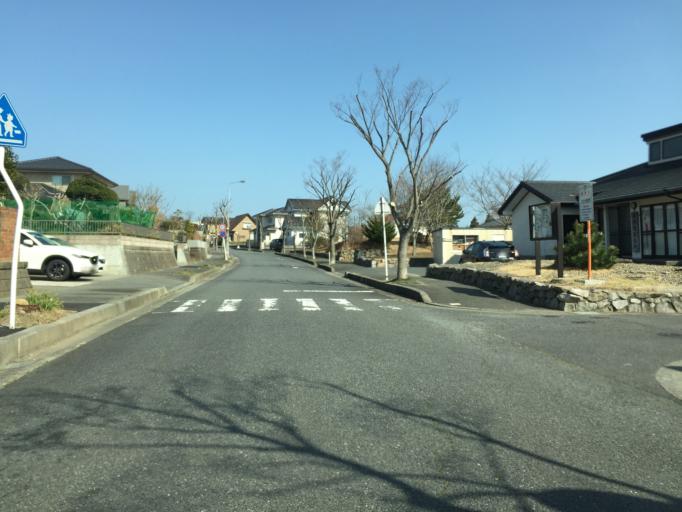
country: JP
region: Fukushima
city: Iwaki
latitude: 36.9677
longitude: 140.9373
